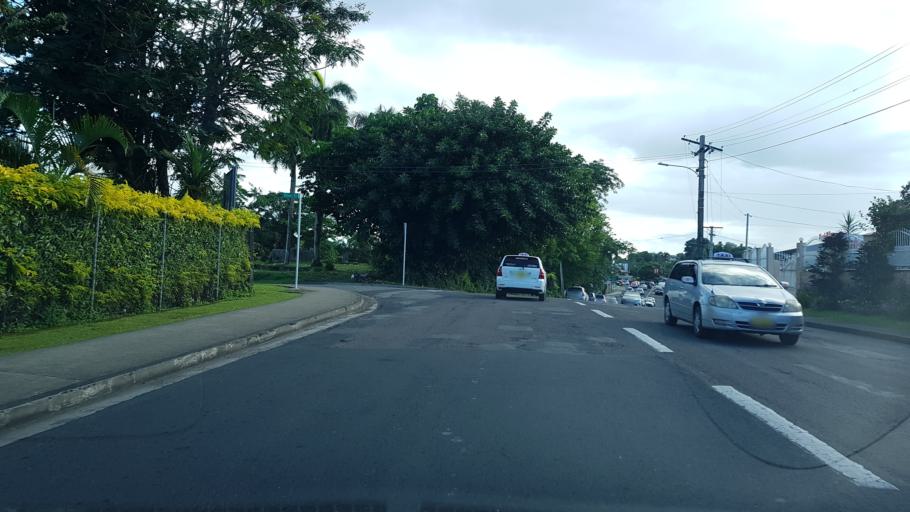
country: FJ
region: Central
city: Suva
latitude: -18.1456
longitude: 178.4334
